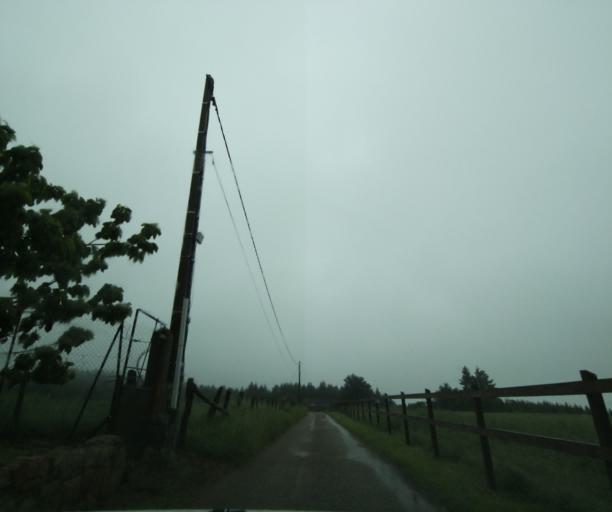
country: FR
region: Bourgogne
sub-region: Departement de Saone-et-Loire
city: Charolles
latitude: 46.3896
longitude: 4.3719
